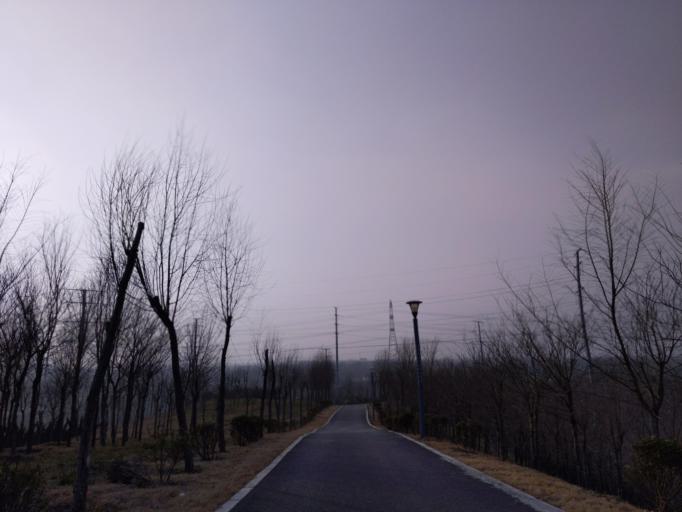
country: CN
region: Henan Sheng
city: Puyang
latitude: 35.8203
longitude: 115.0012
